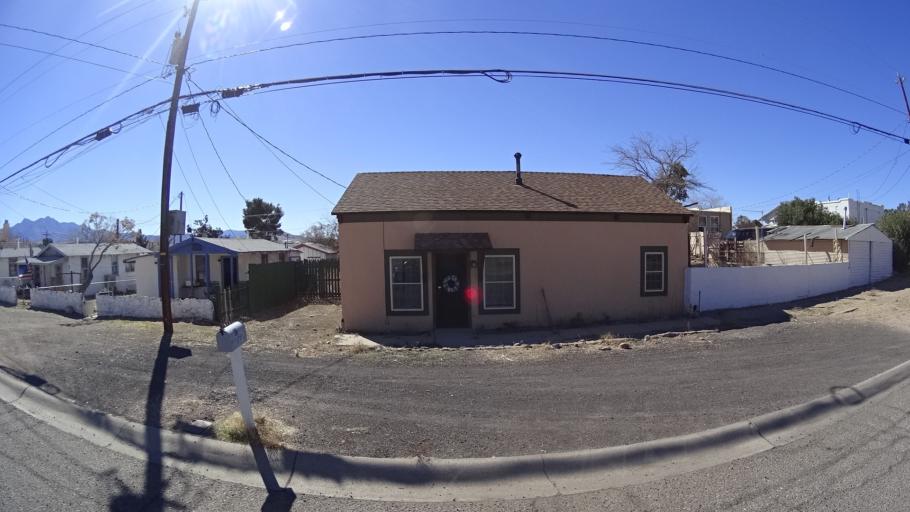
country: US
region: Arizona
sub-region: Mohave County
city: Kingman
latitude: 35.1932
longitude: -114.0553
